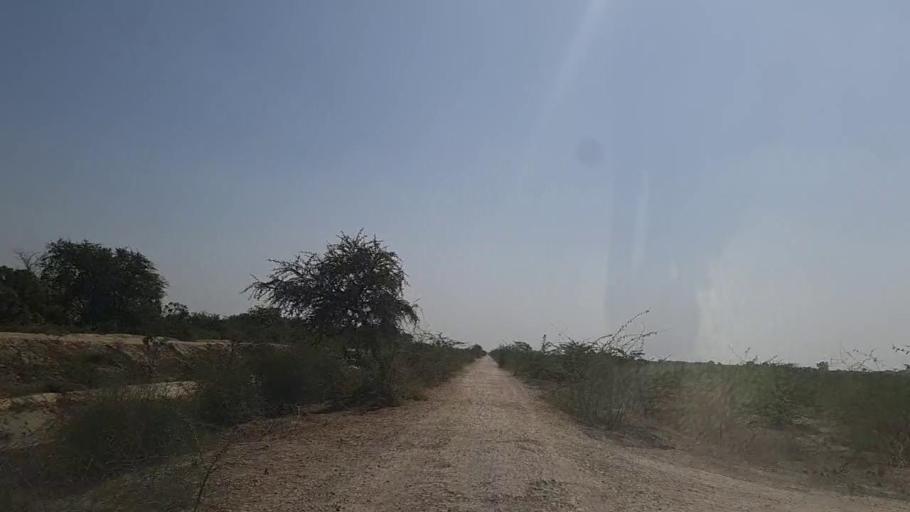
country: PK
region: Sindh
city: Naukot
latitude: 24.6476
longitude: 69.2760
